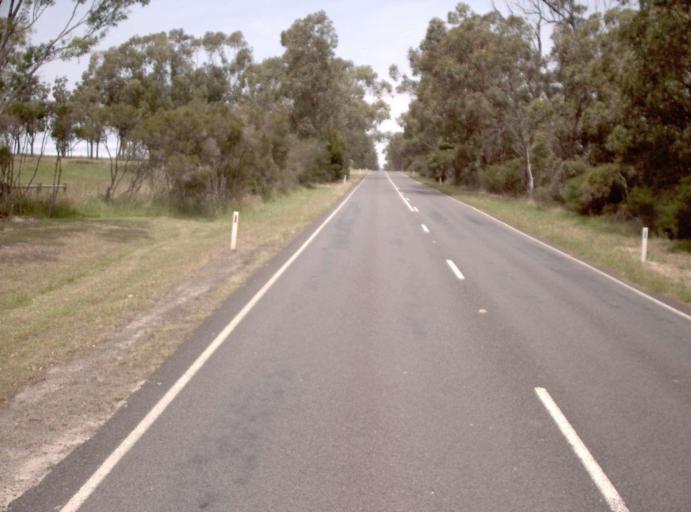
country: AU
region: Victoria
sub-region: Latrobe
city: Traralgon
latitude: -38.5296
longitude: 146.7050
